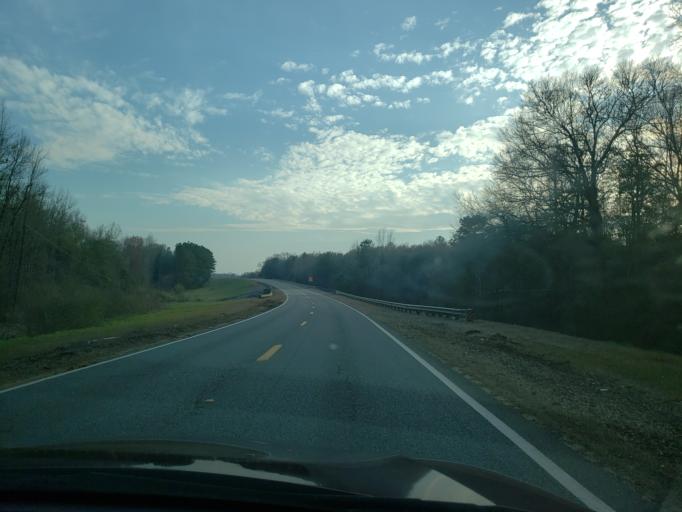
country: US
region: Alabama
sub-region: Hale County
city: Moundville
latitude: 32.9323
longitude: -87.6338
